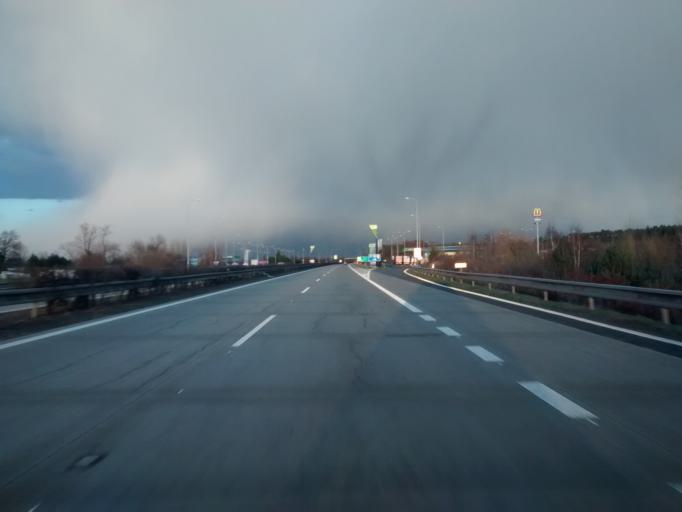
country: CZ
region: Central Bohemia
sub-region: Okres Nymburk
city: Podebrady
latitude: 50.1211
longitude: 15.0782
